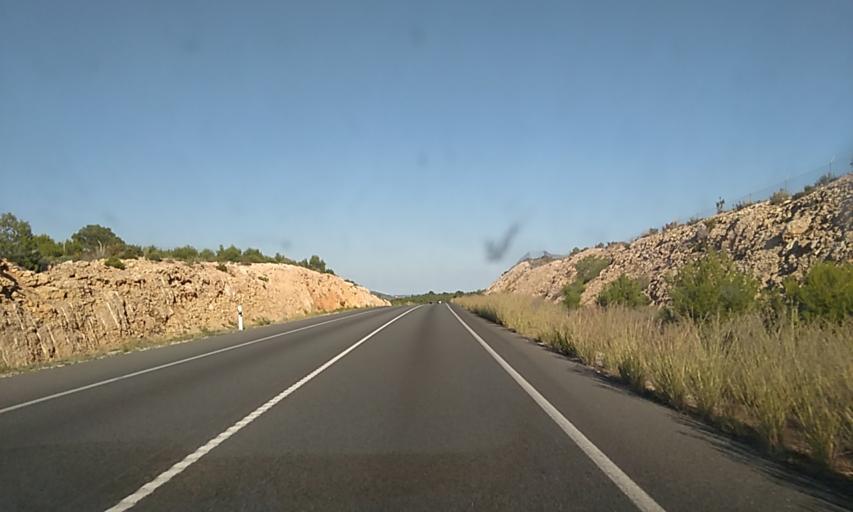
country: ES
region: Valencia
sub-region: Provincia de Castello
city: Torreblanca
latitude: 40.2214
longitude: 0.1684
